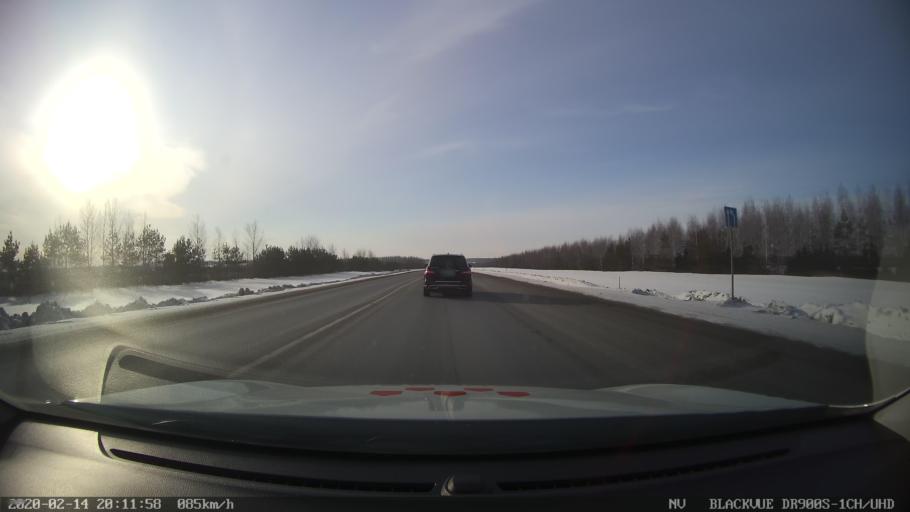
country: RU
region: Tatarstan
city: Verkhniy Uslon
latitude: 55.6711
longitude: 48.8676
